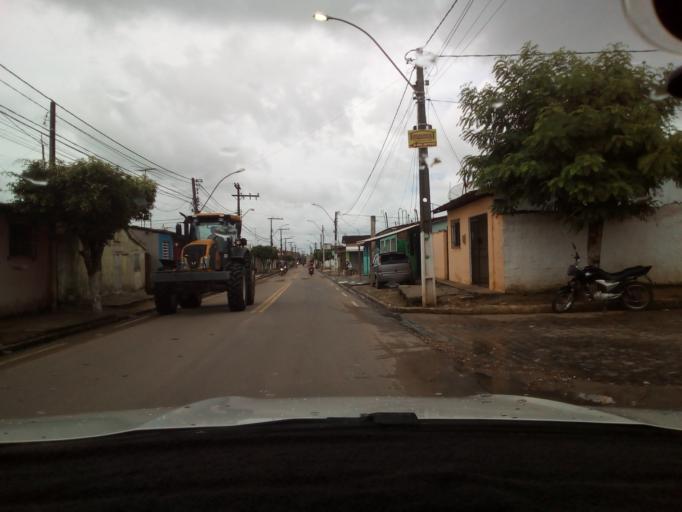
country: BR
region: Paraiba
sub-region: Pedras De Fogo
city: Pedras de Fogo
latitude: -7.4046
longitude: -35.1085
